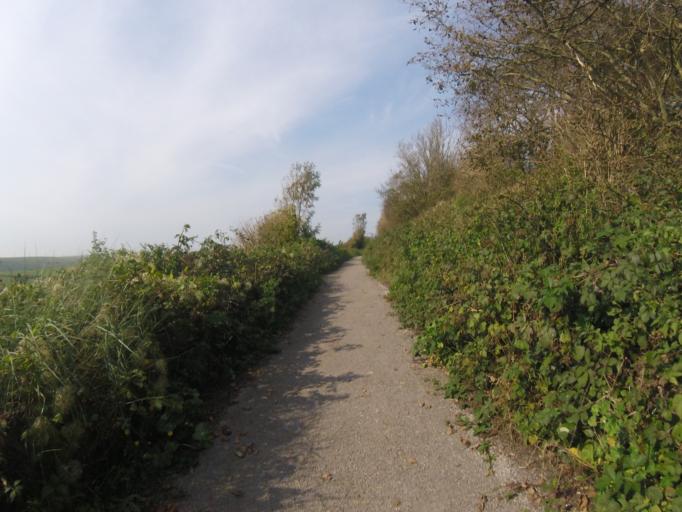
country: GB
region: England
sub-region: East Sussex
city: Portslade
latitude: 50.8600
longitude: -0.2017
